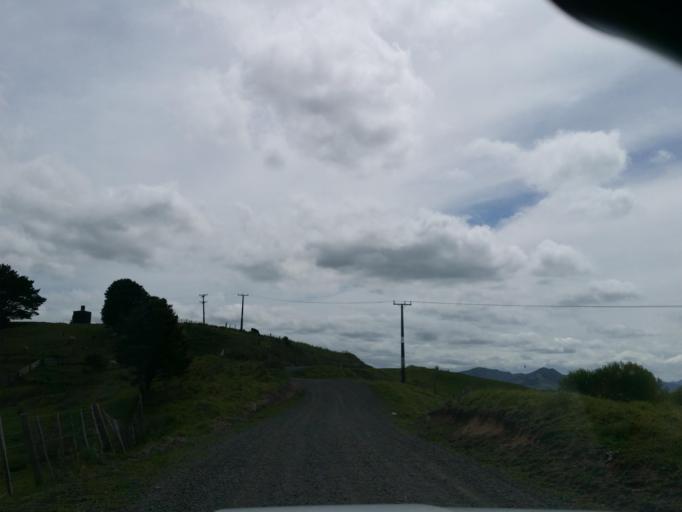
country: NZ
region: Northland
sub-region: Kaipara District
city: Dargaville
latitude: -35.9100
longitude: 174.0329
